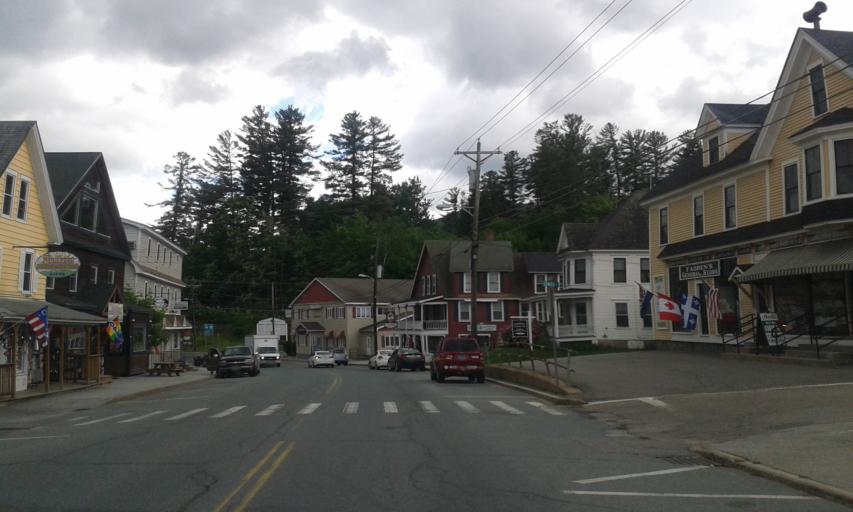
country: US
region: New Hampshire
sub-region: Grafton County
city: Woodstock
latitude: 44.0316
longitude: -71.6867
